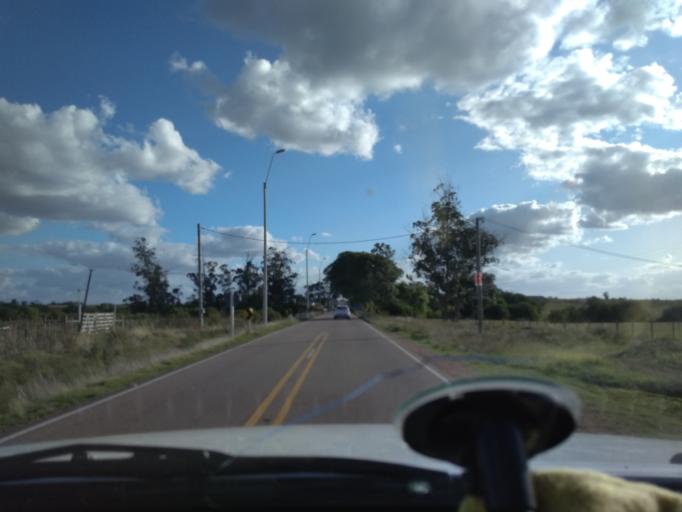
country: UY
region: Canelones
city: Tala
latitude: -34.3639
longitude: -55.7782
